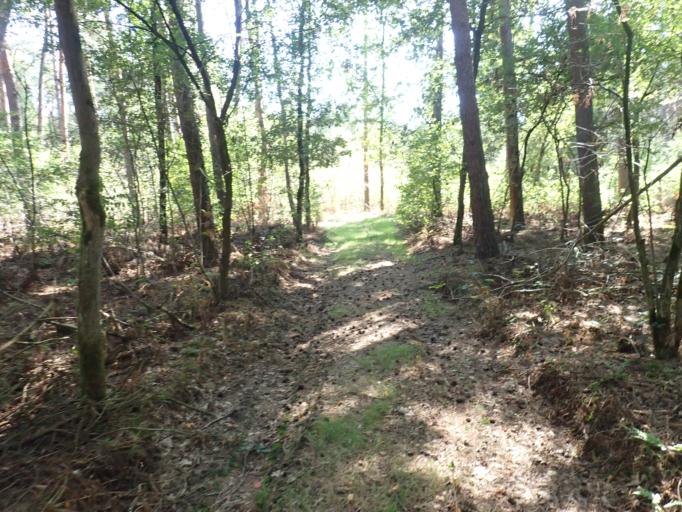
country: BE
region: Flanders
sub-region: Provincie Antwerpen
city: Lille
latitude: 51.2159
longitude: 4.8712
